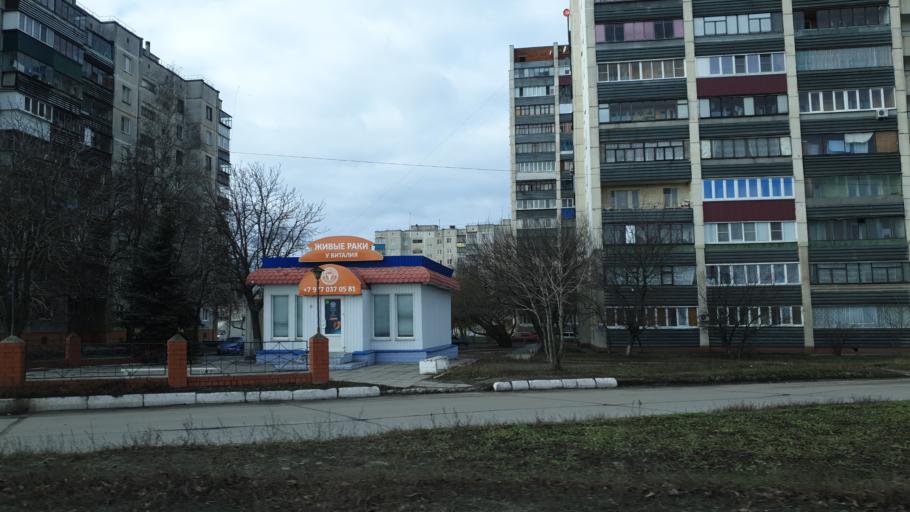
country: RU
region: Kursk
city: Kursk
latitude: 51.6781
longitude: 36.1468
